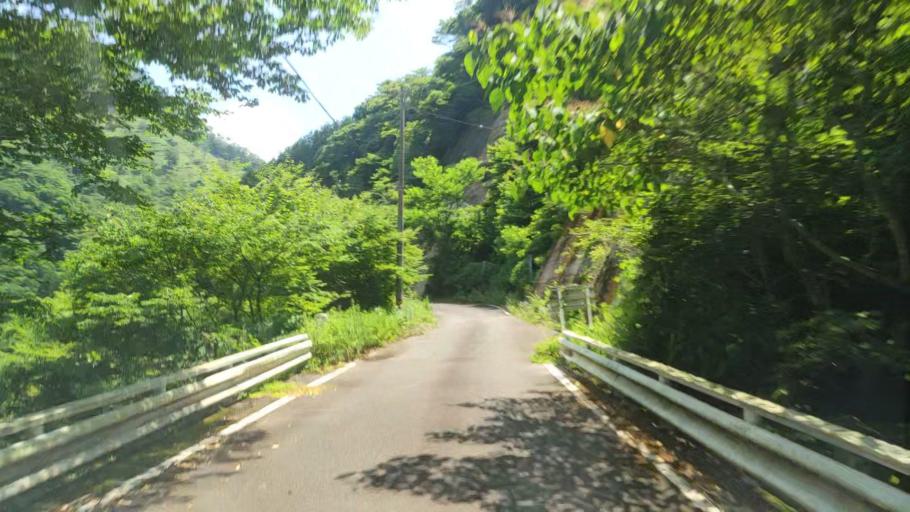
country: JP
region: Fukui
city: Ono
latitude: 35.7418
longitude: 136.5824
